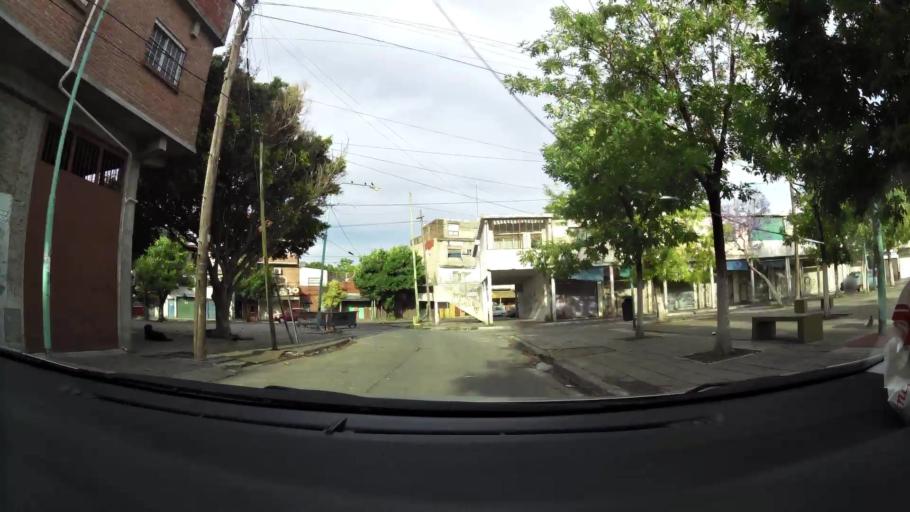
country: AR
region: Buenos Aires F.D.
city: Villa Lugano
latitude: -34.6446
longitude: -58.4410
